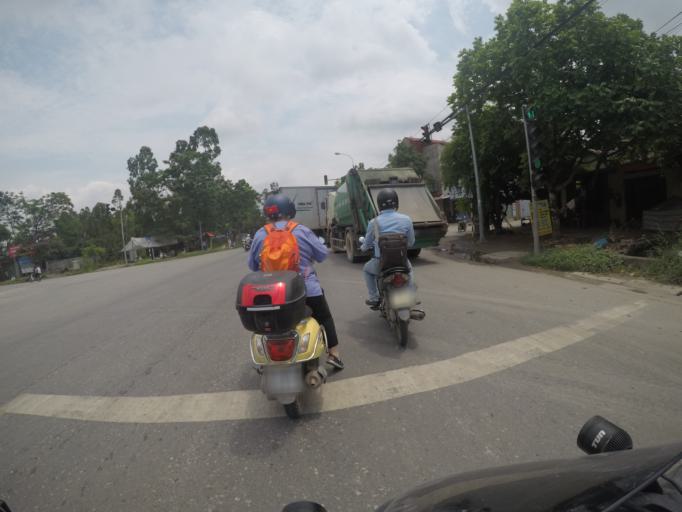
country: VN
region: Ha Noi
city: Soc Son
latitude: 21.2300
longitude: 105.8491
